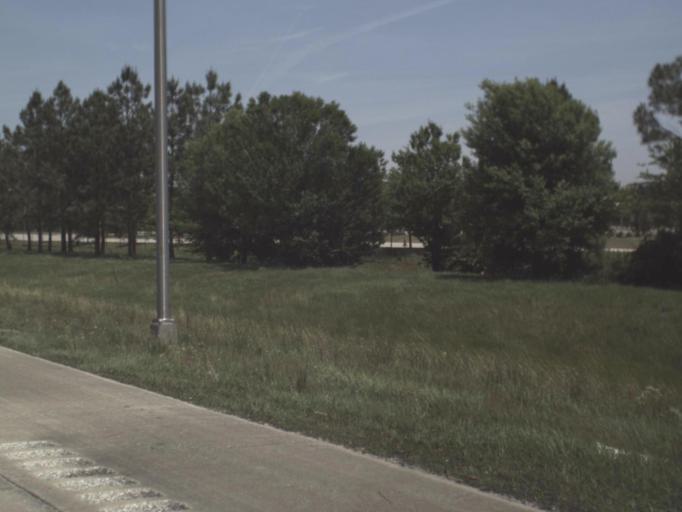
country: US
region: Florida
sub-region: Saint Johns County
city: Palm Valley
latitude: 30.2061
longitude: -81.5137
